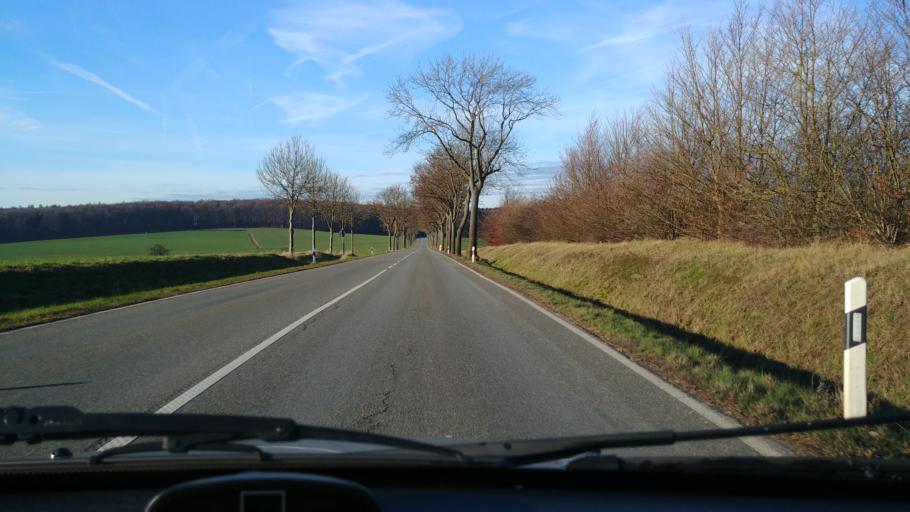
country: DE
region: Rheinland-Pfalz
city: Holzhausen an der Haide
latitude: 50.2219
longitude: 7.9024
